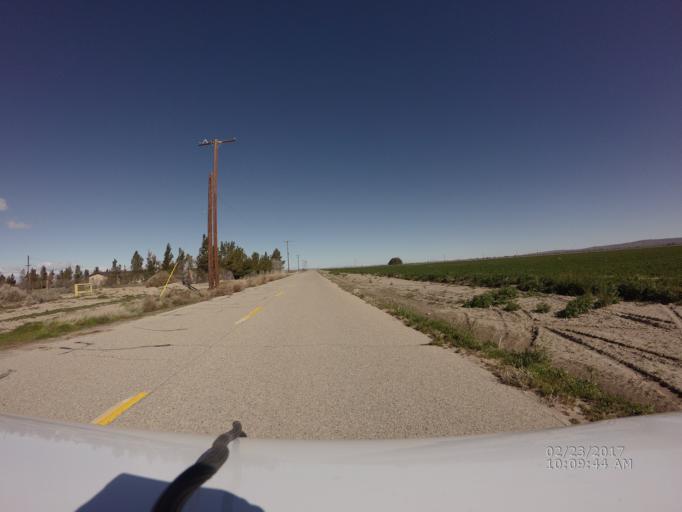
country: US
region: California
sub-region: Los Angeles County
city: Lake Los Angeles
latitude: 34.7157
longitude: -117.9341
